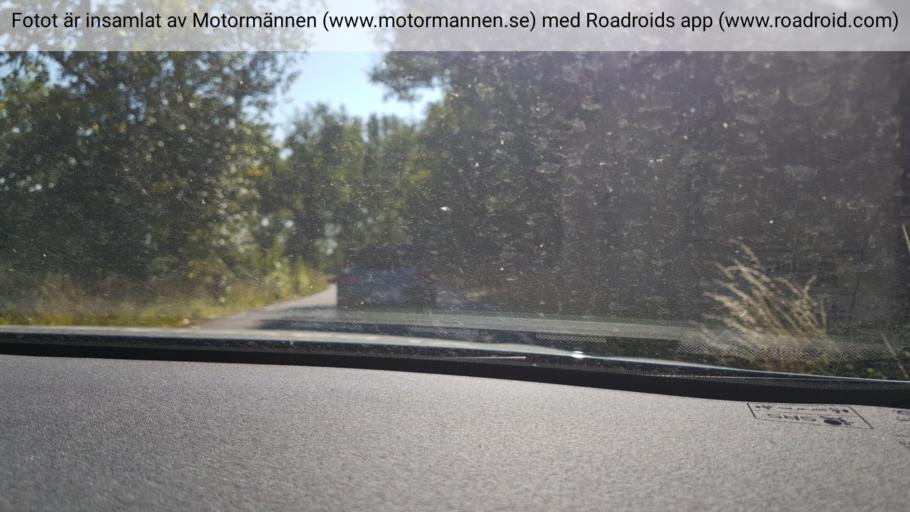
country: SE
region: Vaestra Goetaland
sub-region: Gotene Kommun
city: Kallby
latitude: 58.5575
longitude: 13.3477
